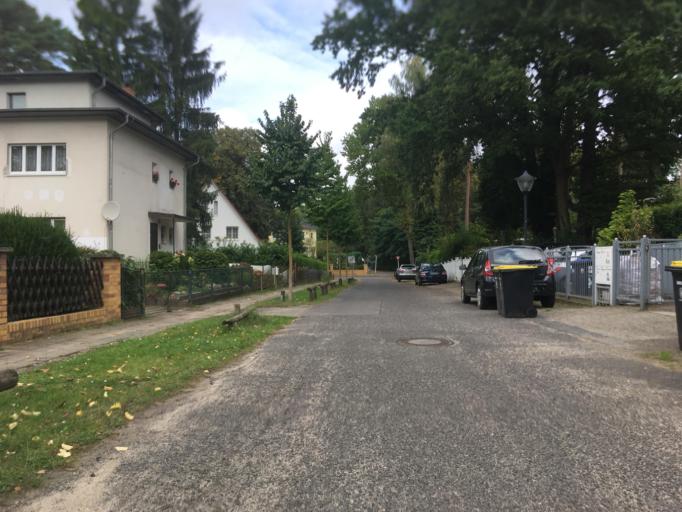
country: DE
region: Brandenburg
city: Glienicke
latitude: 52.6319
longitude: 13.3432
